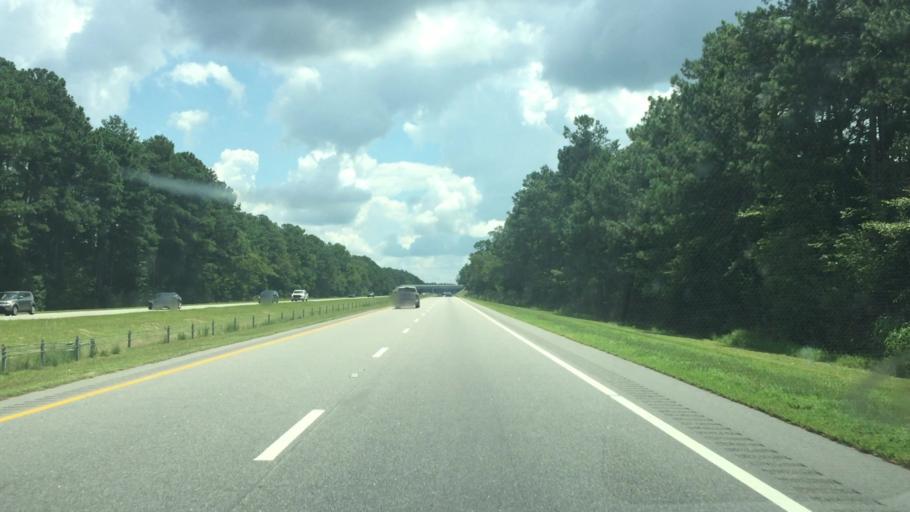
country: US
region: North Carolina
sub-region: Columbus County
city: Chadbourn
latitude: 34.3889
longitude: -78.8784
